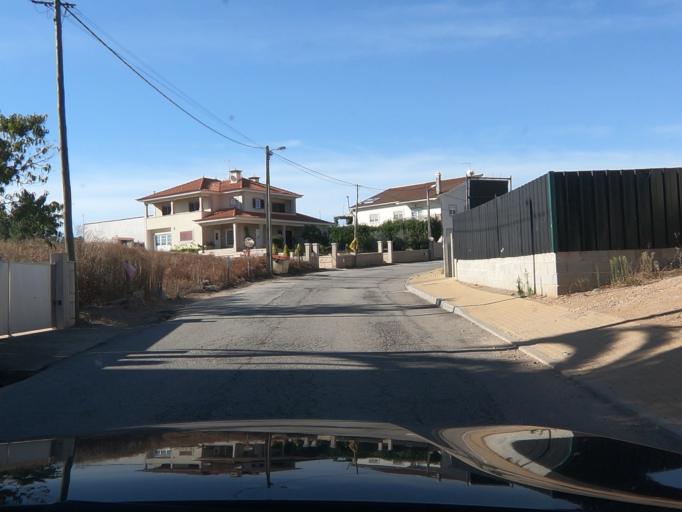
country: PT
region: Vila Real
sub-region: Vila Real
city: Vila Real
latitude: 41.2703
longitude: -7.6941
